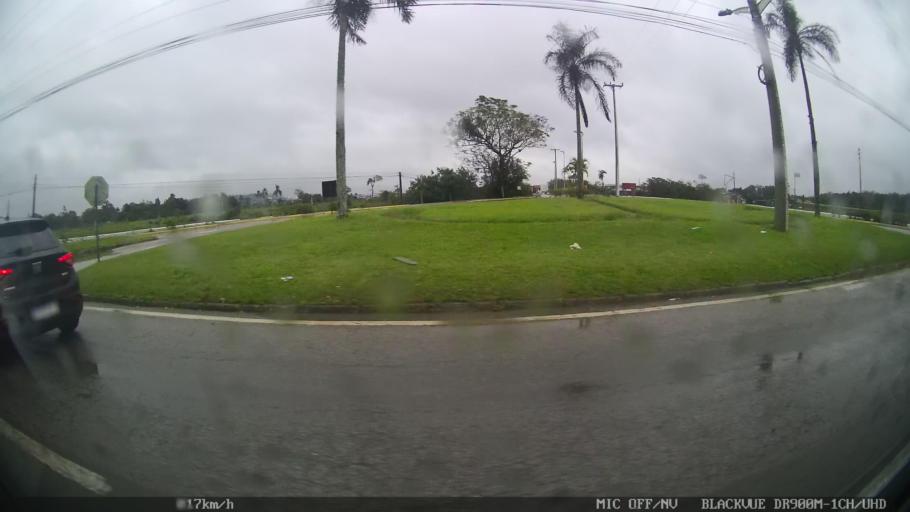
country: BR
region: Santa Catarina
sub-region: Itajai
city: Itajai
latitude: -26.9342
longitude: -48.6919
